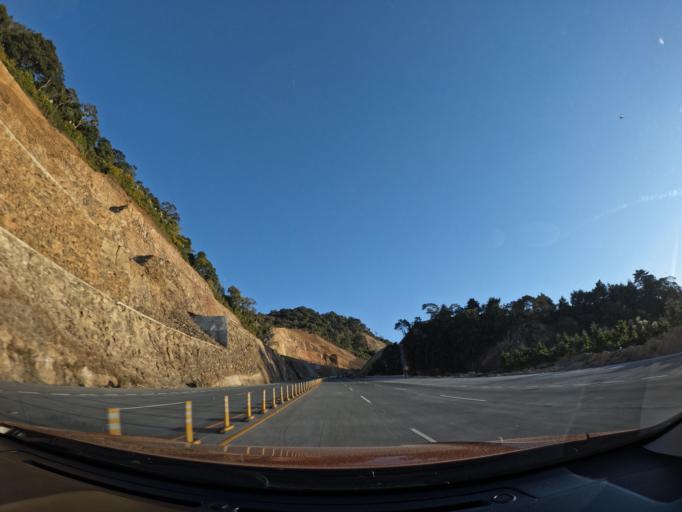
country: GT
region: Guatemala
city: Villa Canales
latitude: 14.4921
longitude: -90.4995
